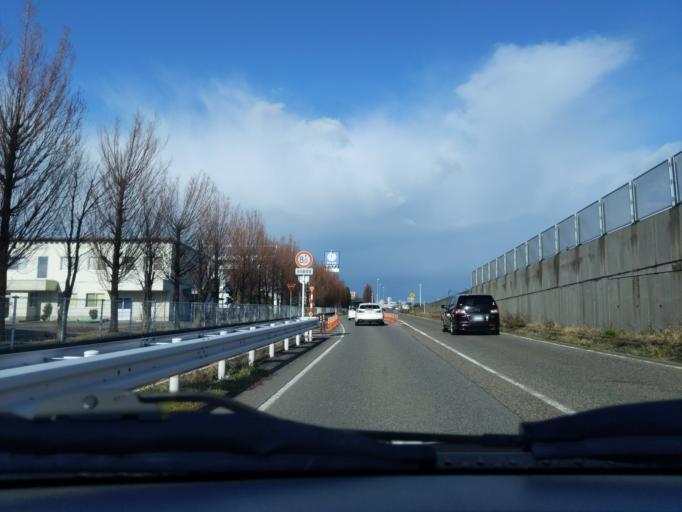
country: JP
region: Niigata
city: Kameda-honcho
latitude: 37.8709
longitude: 139.0869
